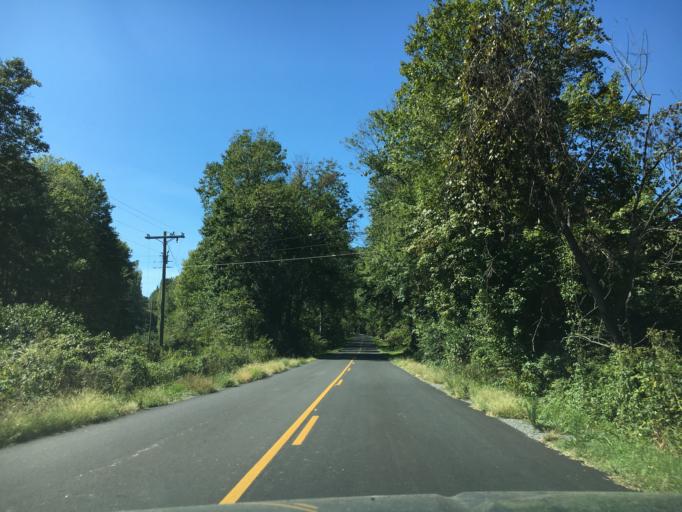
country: US
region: Virginia
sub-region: Albemarle County
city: Crozet
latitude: 37.9798
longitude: -78.6868
